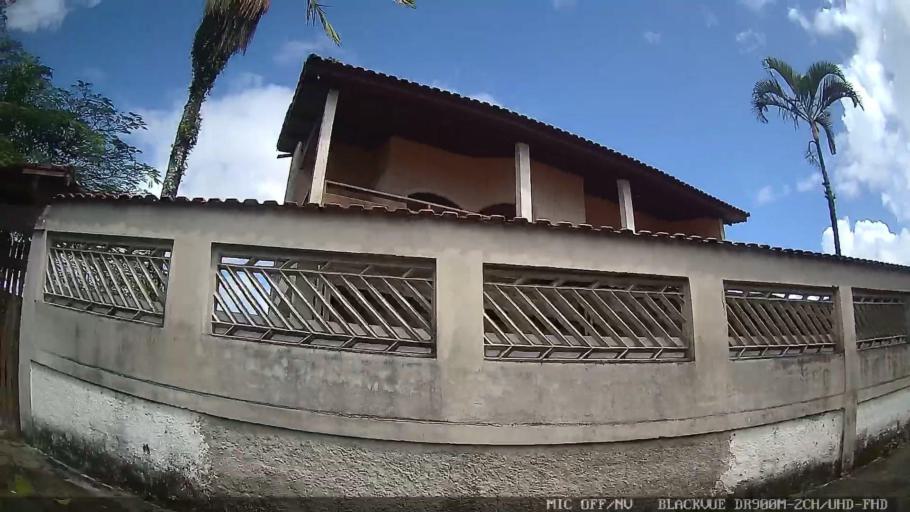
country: BR
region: Sao Paulo
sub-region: Itanhaem
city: Itanhaem
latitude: -24.1882
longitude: -46.8124
